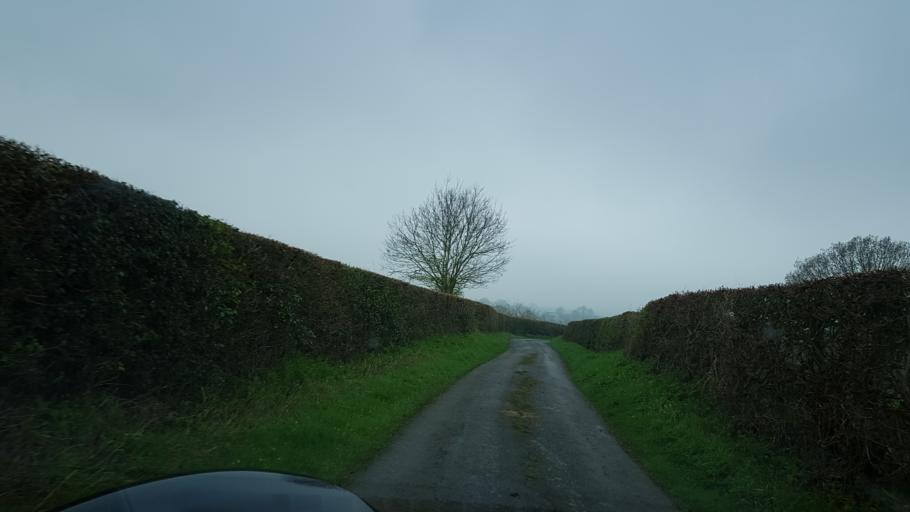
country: GB
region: England
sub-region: Herefordshire
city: Yatton
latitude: 52.0195
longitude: -2.5236
